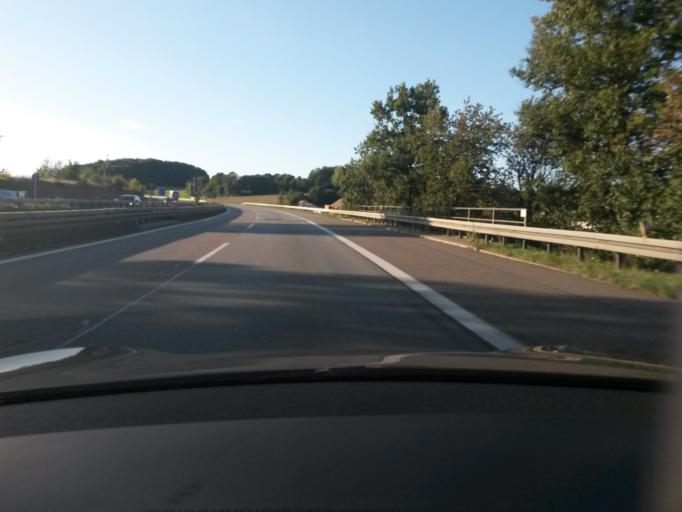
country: DE
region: Bavaria
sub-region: Upper Palatinate
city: Brunn
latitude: 49.0823
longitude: 11.9020
